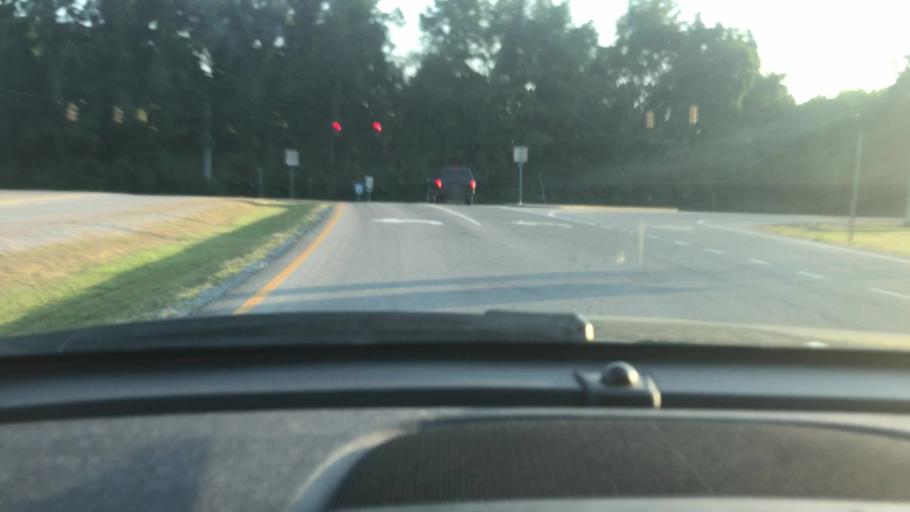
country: US
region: Tennessee
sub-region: Dickson County
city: Dickson
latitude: 36.0836
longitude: -87.3807
